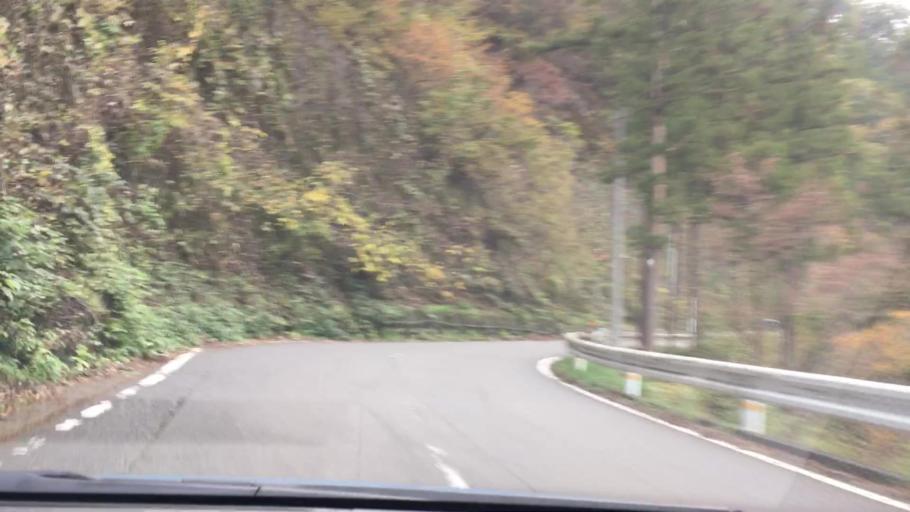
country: JP
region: Yamanashi
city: Uenohara
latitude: 35.5547
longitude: 139.1386
